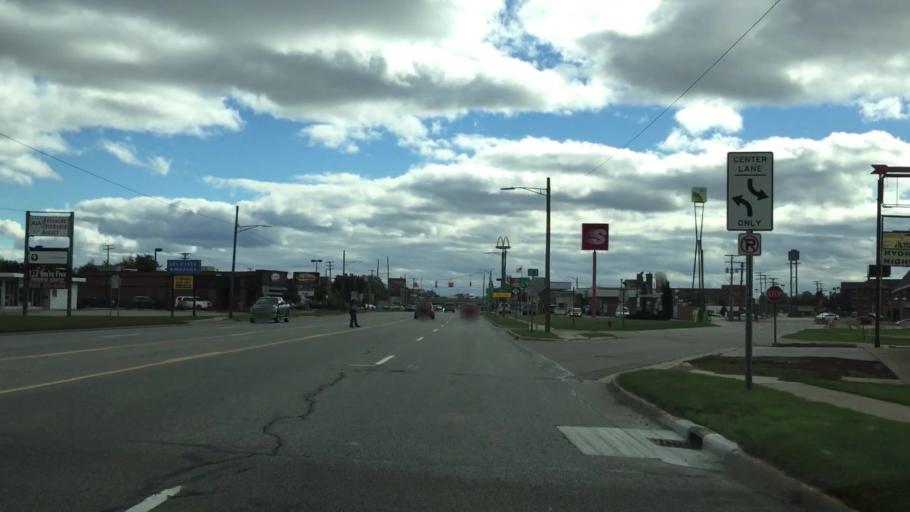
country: US
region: Michigan
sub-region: Saint Clair County
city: Port Huron
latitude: 43.0033
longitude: -82.4405
